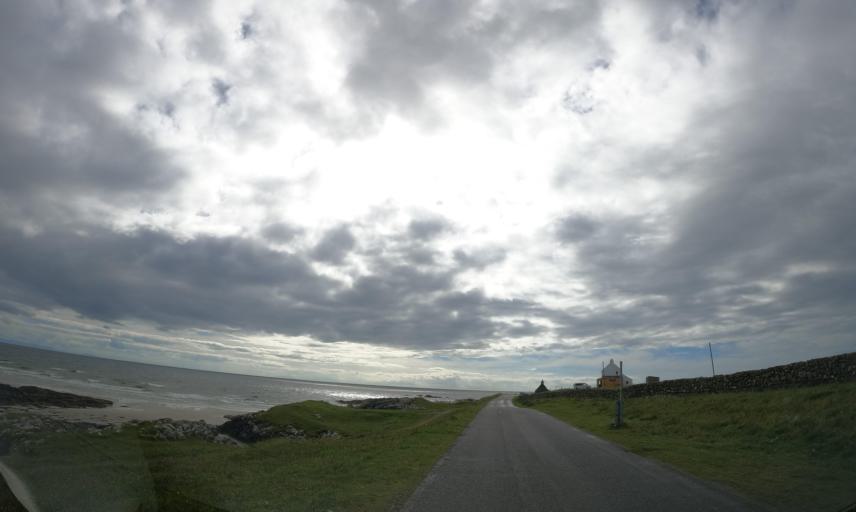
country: GB
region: Scotland
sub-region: Eilean Siar
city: Barra
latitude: 56.4873
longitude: -6.8792
